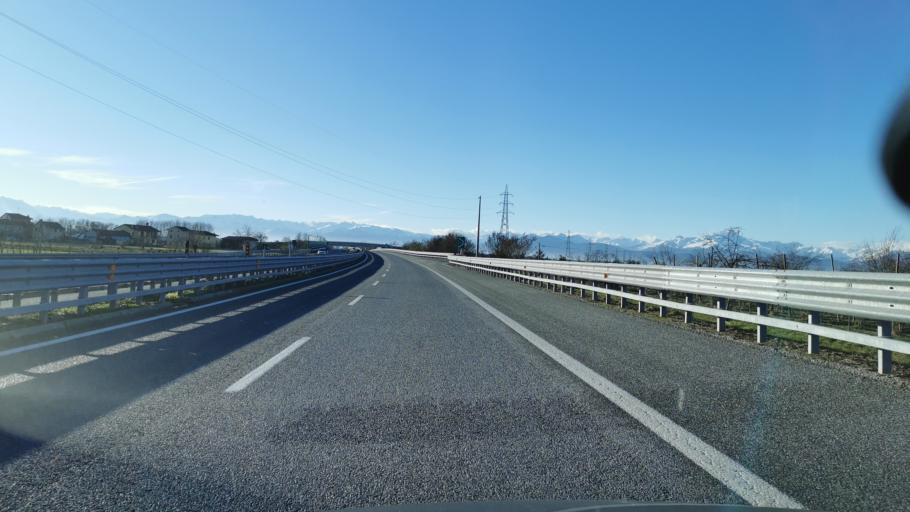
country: IT
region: Piedmont
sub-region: Provincia di Cuneo
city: Sant'Albano Stura
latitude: 44.4706
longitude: 7.7372
